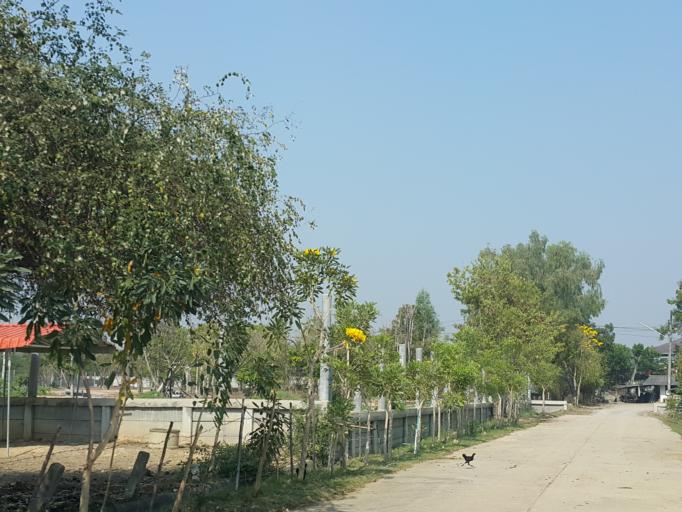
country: TH
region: Chiang Mai
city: San Kamphaeng
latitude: 18.7904
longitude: 99.0785
